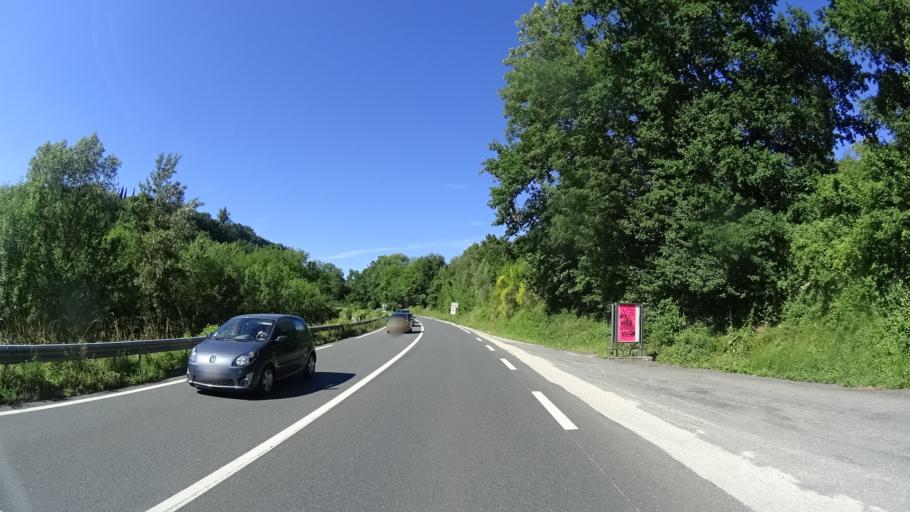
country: FR
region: Midi-Pyrenees
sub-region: Departement de l'Aveyron
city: Capdenac-Gare
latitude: 44.5835
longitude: 2.0685
